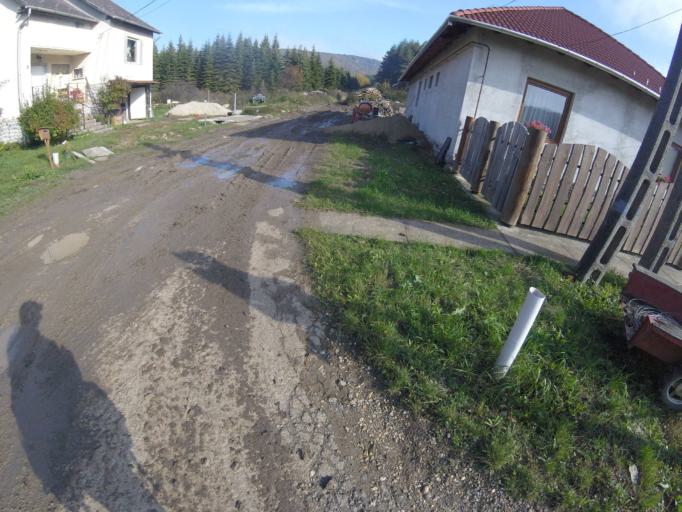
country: HU
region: Borsod-Abauj-Zemplen
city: Putnok
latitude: 48.2183
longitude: 20.4394
